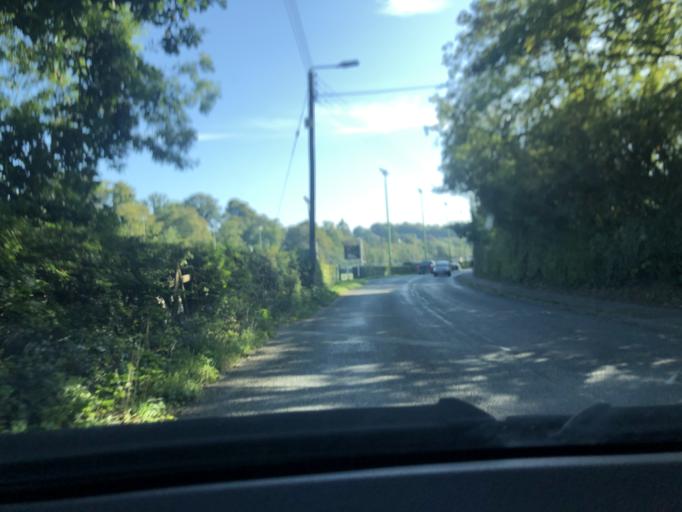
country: GB
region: England
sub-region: Devon
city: Tavistock
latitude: 50.5572
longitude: -4.1299
